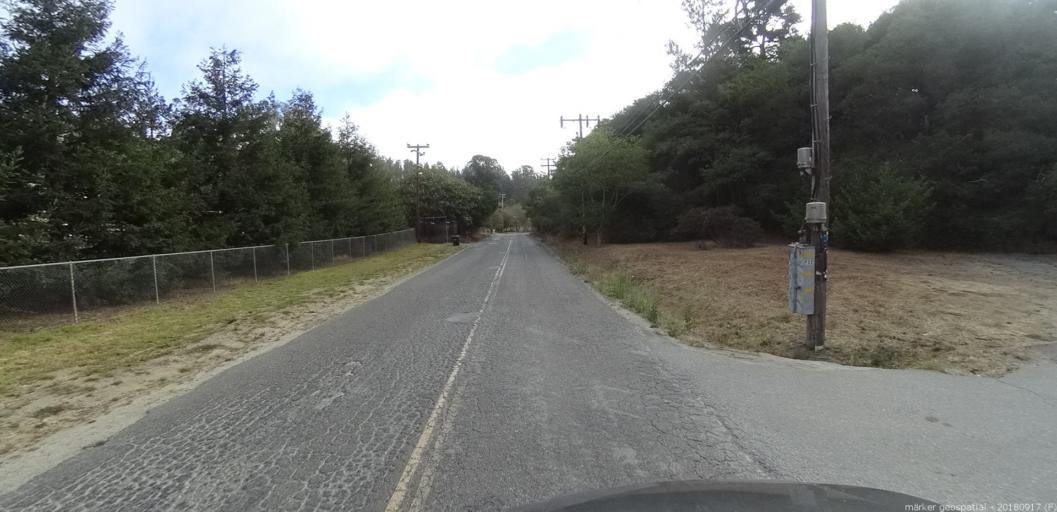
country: US
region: California
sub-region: Monterey County
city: Elkhorn
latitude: 36.8146
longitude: -121.7009
